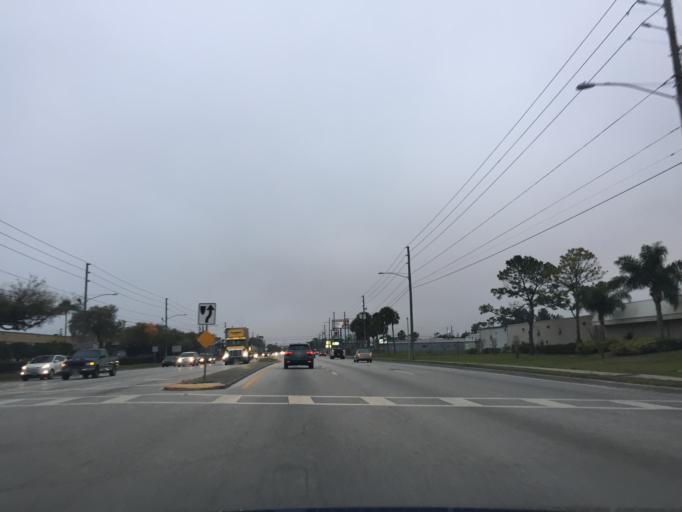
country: US
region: Florida
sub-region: Pinellas County
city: South Highpoint
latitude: 27.8993
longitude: -82.7005
